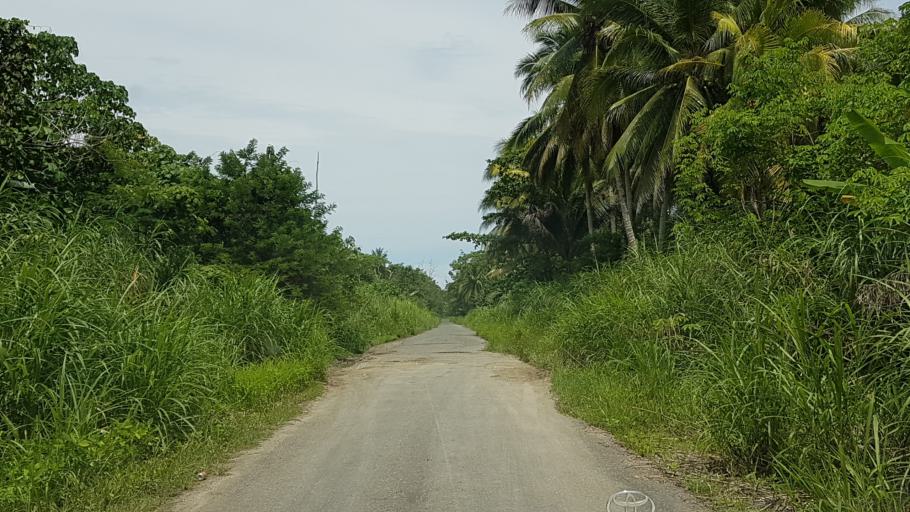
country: PG
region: Madang
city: Madang
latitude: -4.5642
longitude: 145.5058
